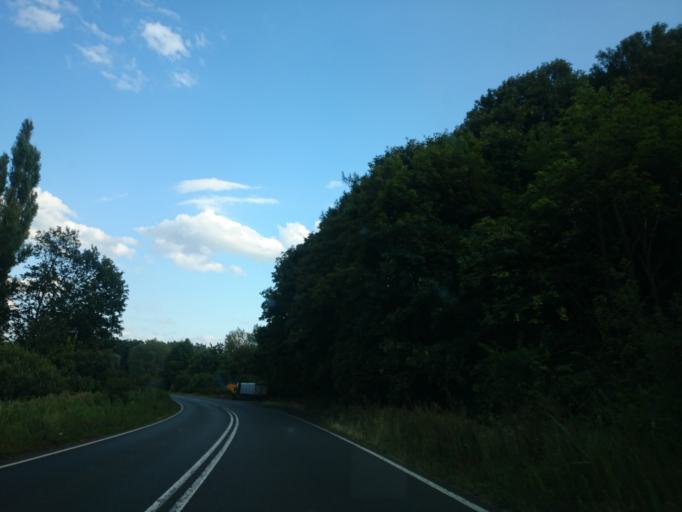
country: PL
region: West Pomeranian Voivodeship
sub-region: Powiat pyrzycki
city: Lipiany
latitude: 52.9923
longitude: 14.9713
